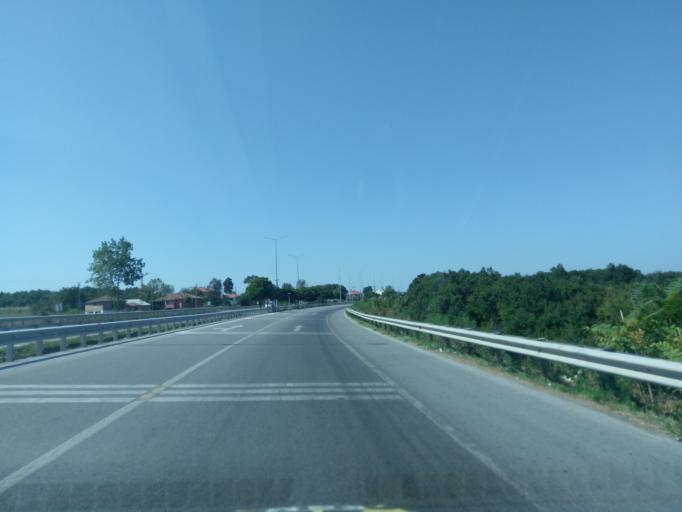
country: TR
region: Samsun
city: Bafra
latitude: 41.5270
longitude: 35.9556
